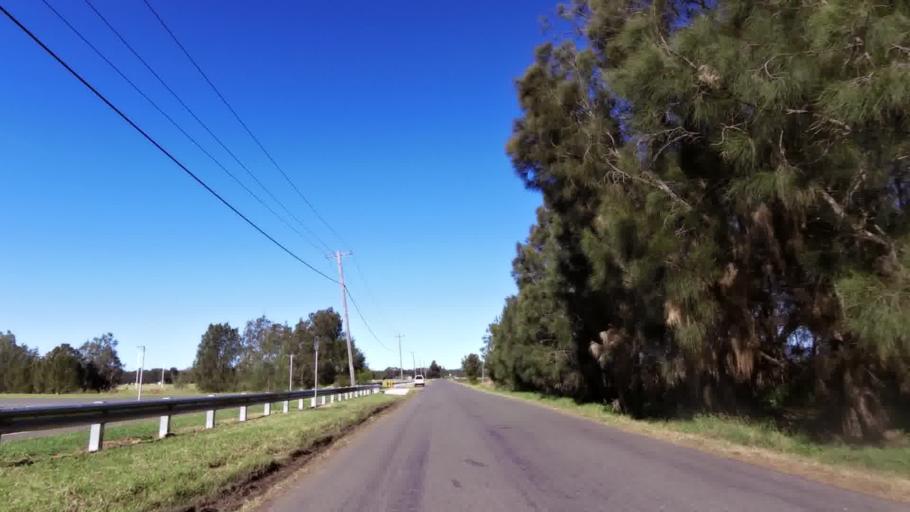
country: AU
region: New South Wales
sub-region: Wollongong
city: Berkeley
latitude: -34.4790
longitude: 150.8337
